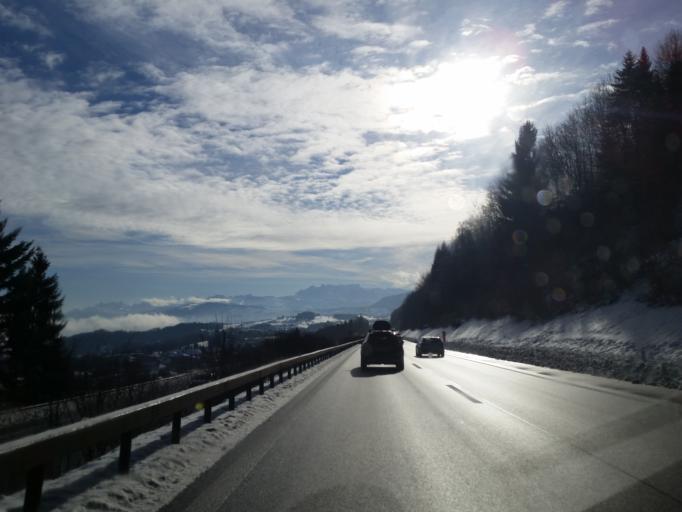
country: CH
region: Zurich
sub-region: Bezirk Horgen
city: Horgen / Oberdorf
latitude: 47.2532
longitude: 8.5903
